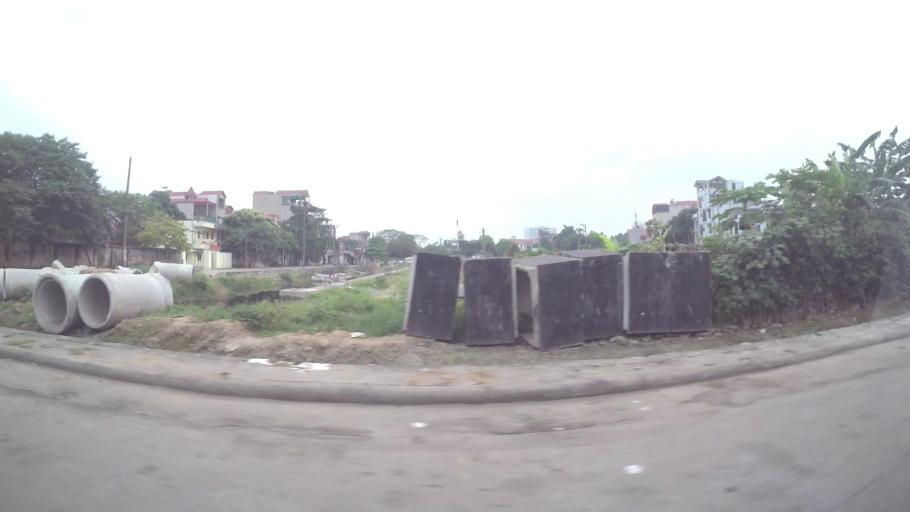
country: VN
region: Ha Noi
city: Hoan Kiem
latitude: 21.0656
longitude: 105.8856
